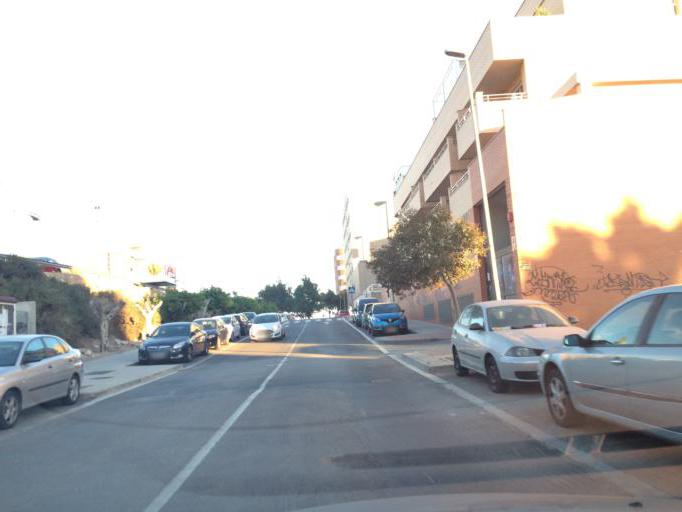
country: ES
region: Andalusia
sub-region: Provincia de Almeria
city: Almeria
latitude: 36.8522
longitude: -2.4482
